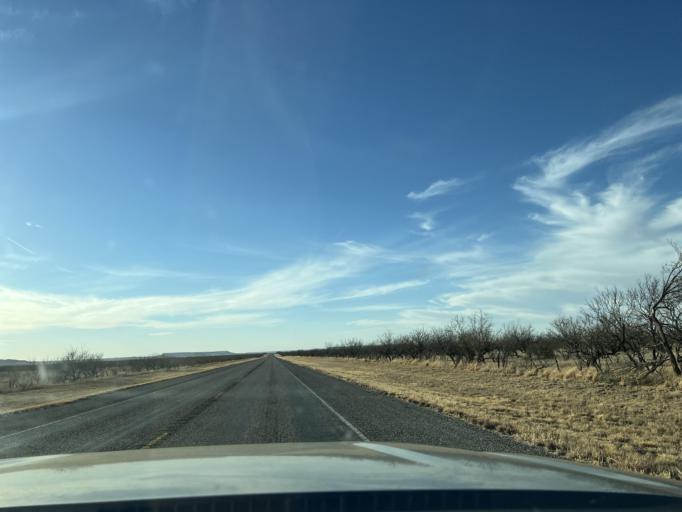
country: US
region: Texas
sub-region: Borden County
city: Gail
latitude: 32.7669
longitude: -101.2977
